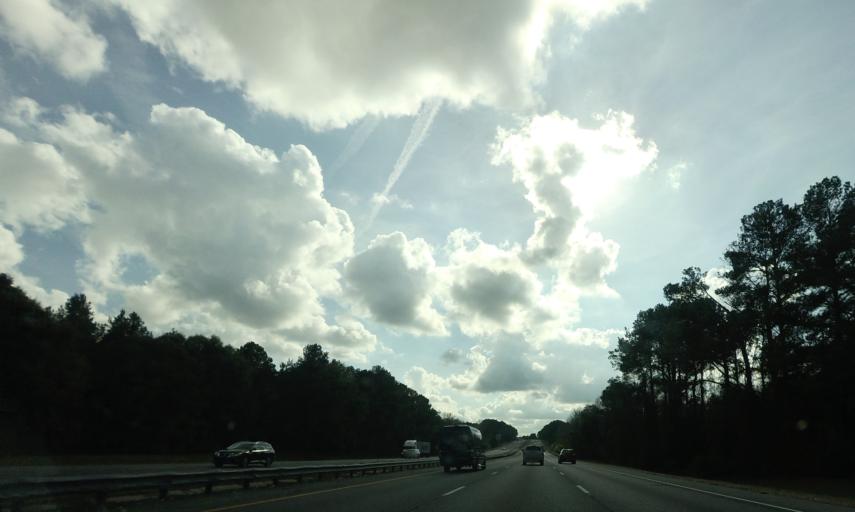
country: US
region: Georgia
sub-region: Houston County
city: Perry
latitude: 32.4216
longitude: -83.7602
